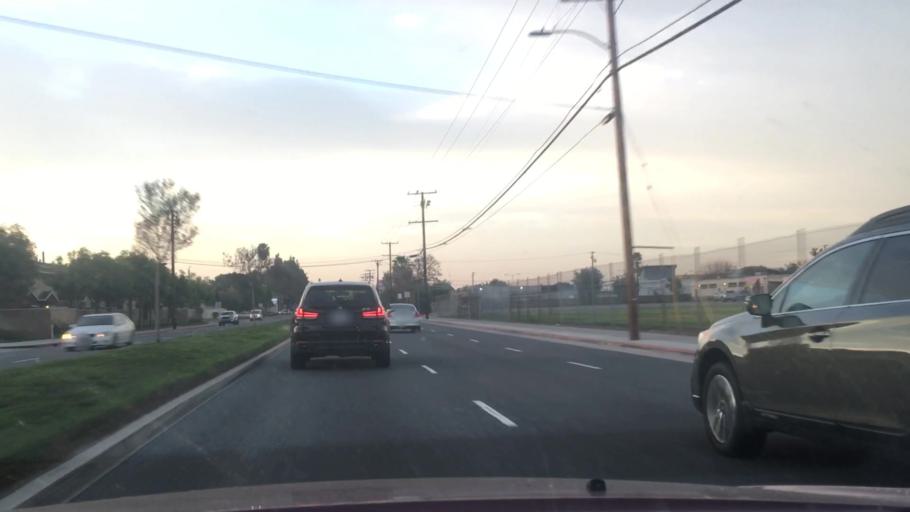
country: US
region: California
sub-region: Orange County
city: Buena Park
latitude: 33.8498
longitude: -118.0112
